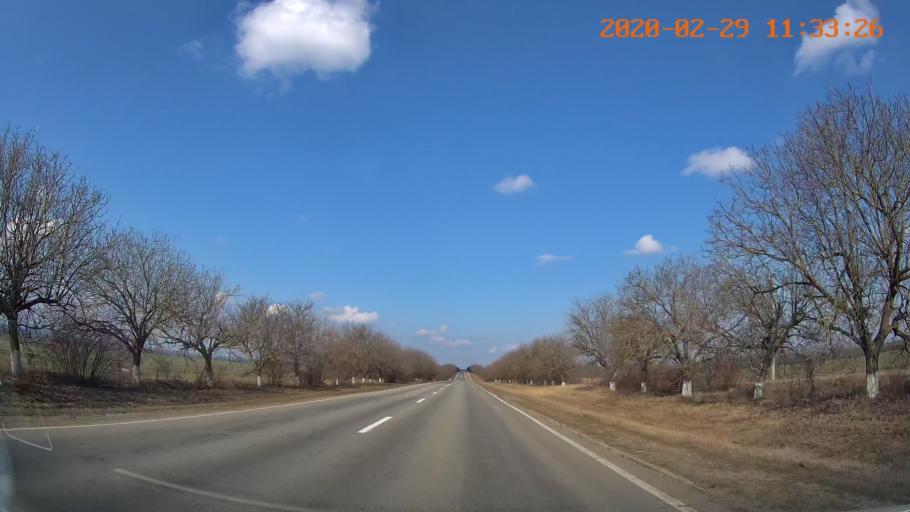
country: MD
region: Rezina
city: Saharna
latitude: 47.5515
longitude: 29.0845
